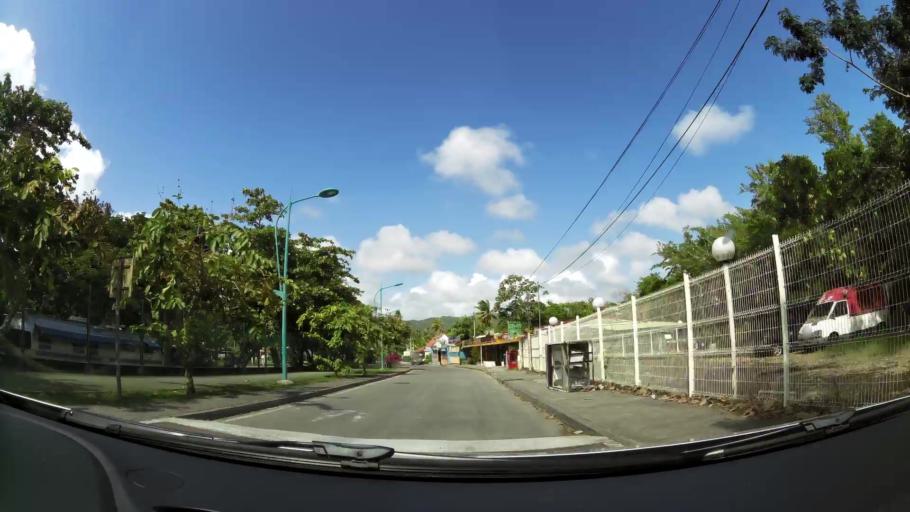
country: MQ
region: Martinique
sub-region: Martinique
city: Le Marin
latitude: 14.4437
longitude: -60.8801
